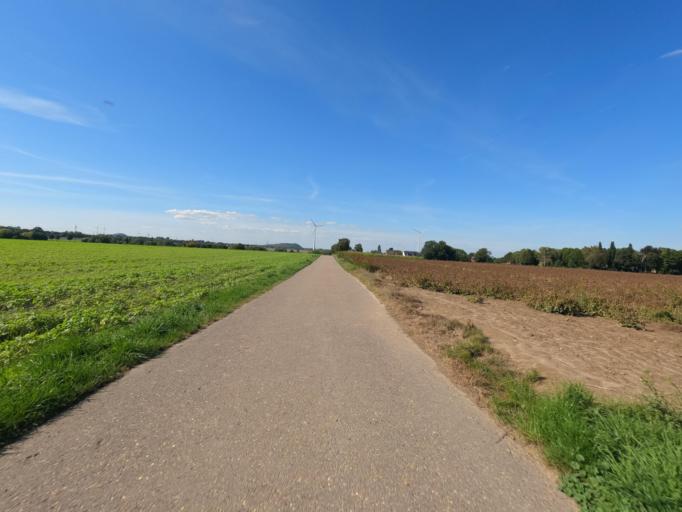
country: DE
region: North Rhine-Westphalia
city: Siersdorf
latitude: 50.8906
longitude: 6.2221
